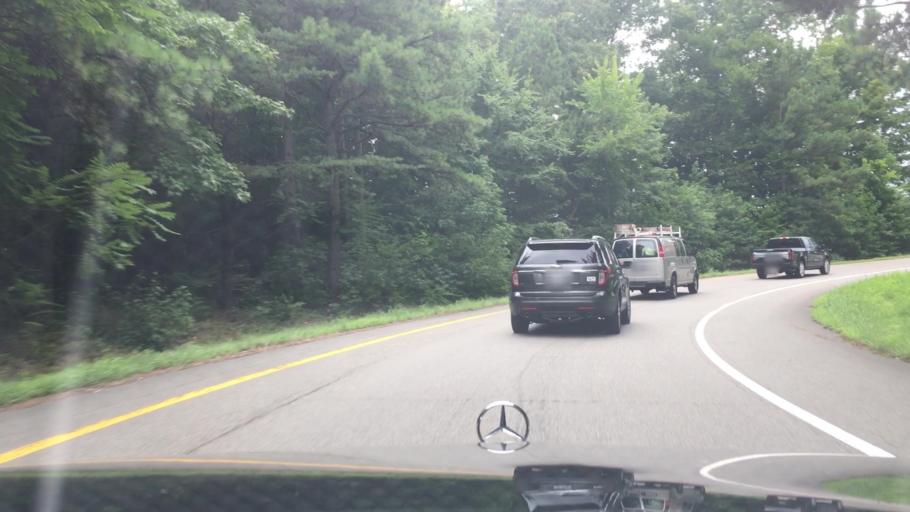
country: US
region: Virginia
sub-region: Chesterfield County
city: Brandermill
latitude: 37.4230
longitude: -77.6282
